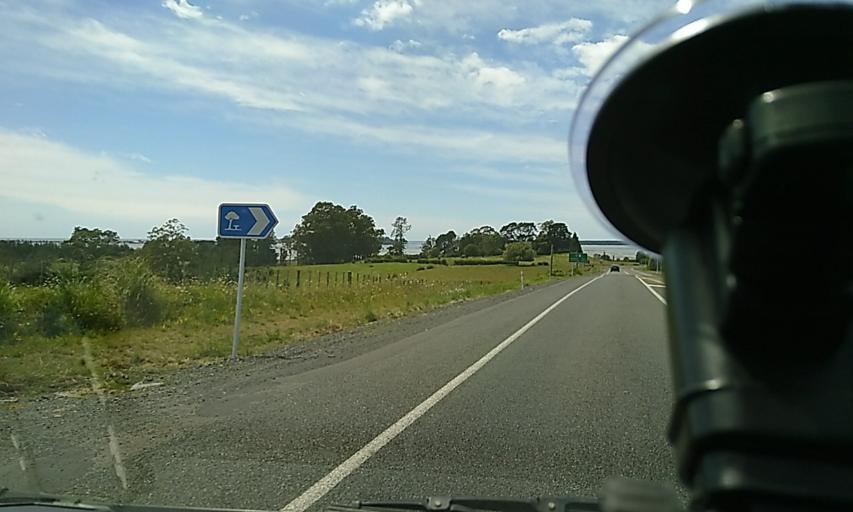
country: NZ
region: Bay of Plenty
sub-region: Western Bay of Plenty District
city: Waihi Beach
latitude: -37.4605
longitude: 175.9325
